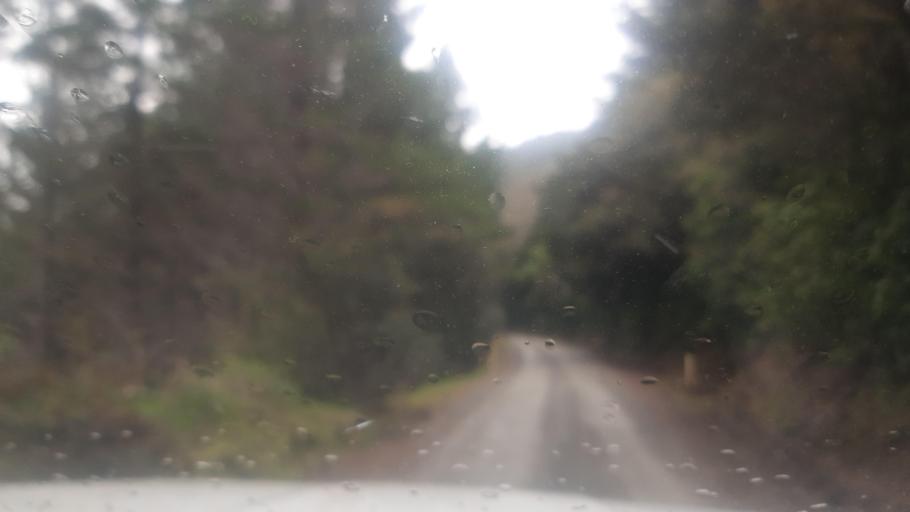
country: NZ
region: Northland
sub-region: Far North District
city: Taipa
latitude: -35.0852
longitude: 173.3907
